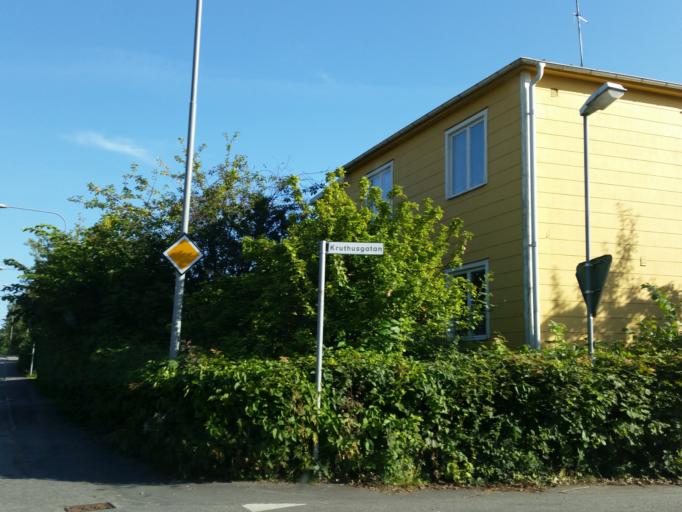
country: SE
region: Soedermanland
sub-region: Trosa Kommun
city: Trosa
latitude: 58.8961
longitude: 17.5506
